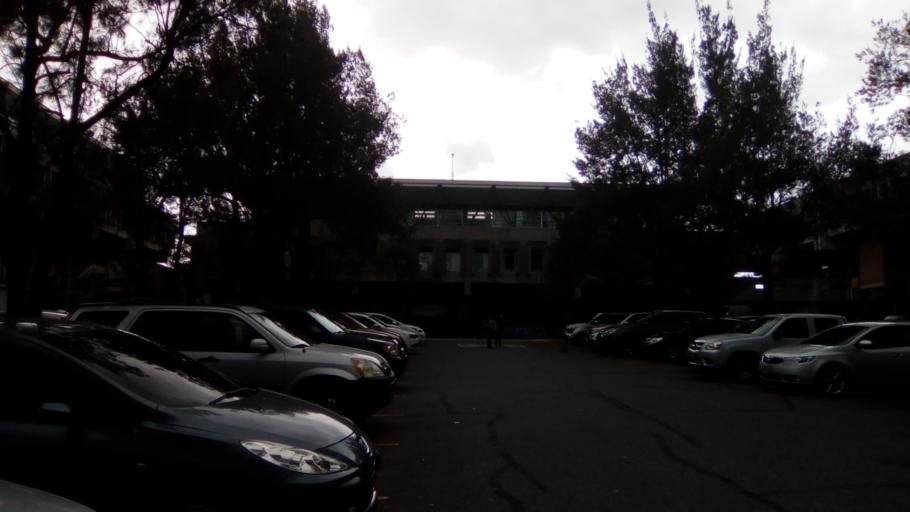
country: GT
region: Guatemala
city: Santa Catarina Pinula
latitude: 14.5950
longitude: -90.4832
